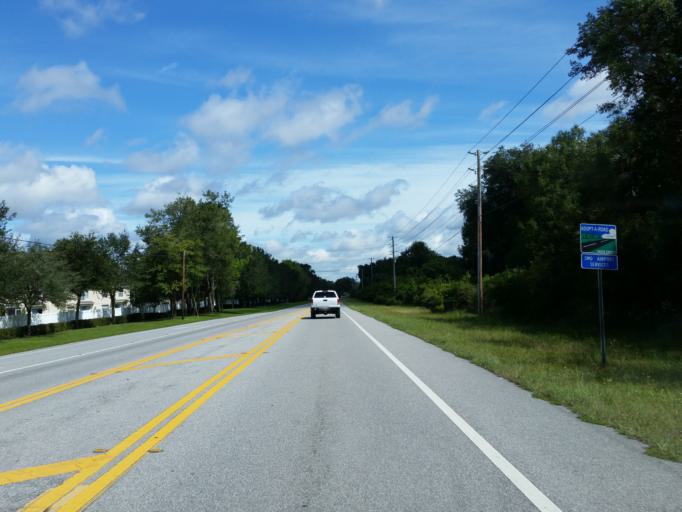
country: US
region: Florida
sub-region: Pasco County
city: Wesley Chapel
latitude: 28.2167
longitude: -82.3887
